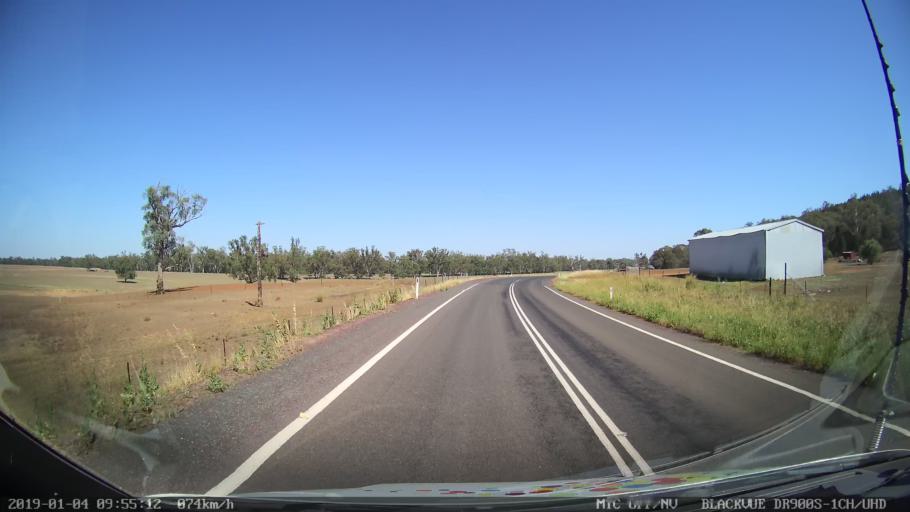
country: AU
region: New South Wales
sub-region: Cabonne
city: Canowindra
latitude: -33.5359
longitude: 148.4060
